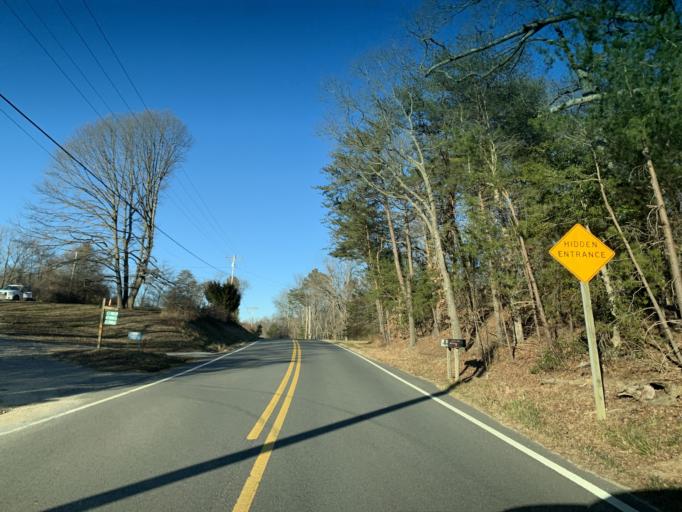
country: US
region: Maryland
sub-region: Saint Mary's County
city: Golden Beach
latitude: 38.4355
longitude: -76.6826
